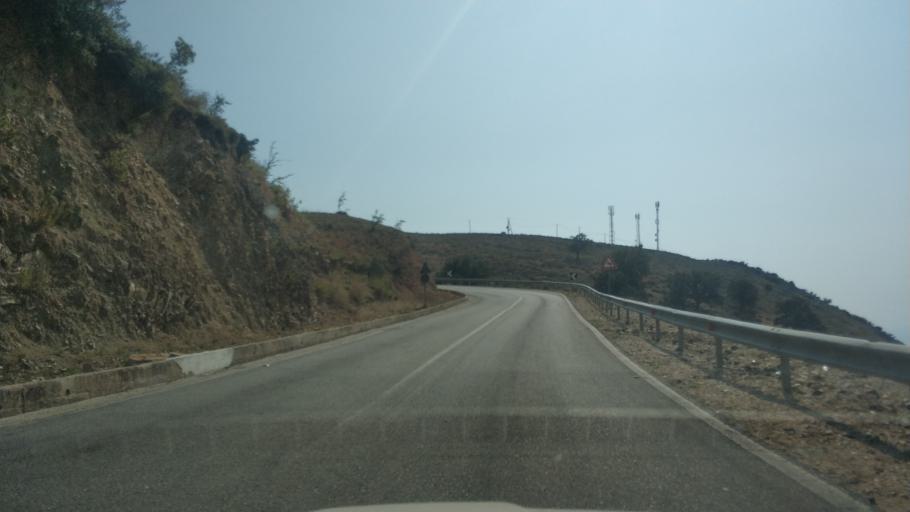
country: AL
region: Vlore
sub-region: Rrethi i Sarandes
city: Lukove
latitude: 40.0438
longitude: 19.8755
